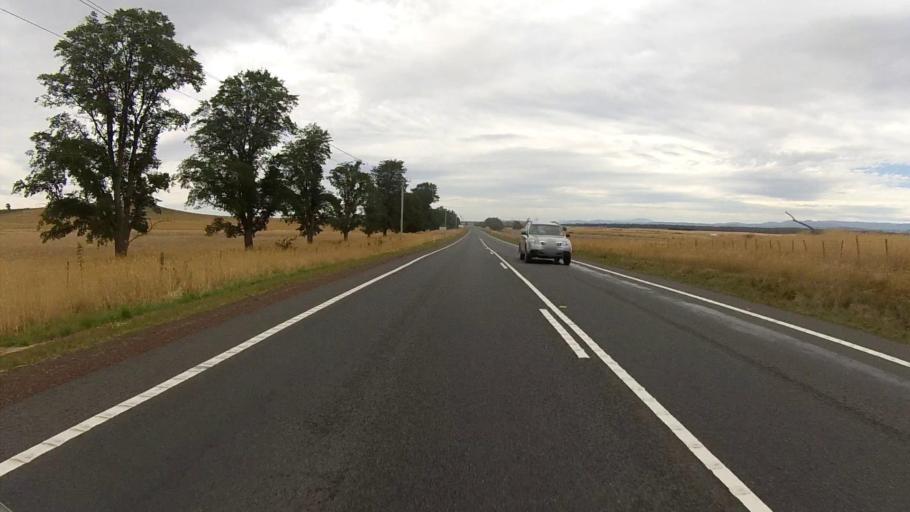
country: AU
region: Tasmania
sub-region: Northern Midlands
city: Evandale
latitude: -41.9048
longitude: 147.4783
